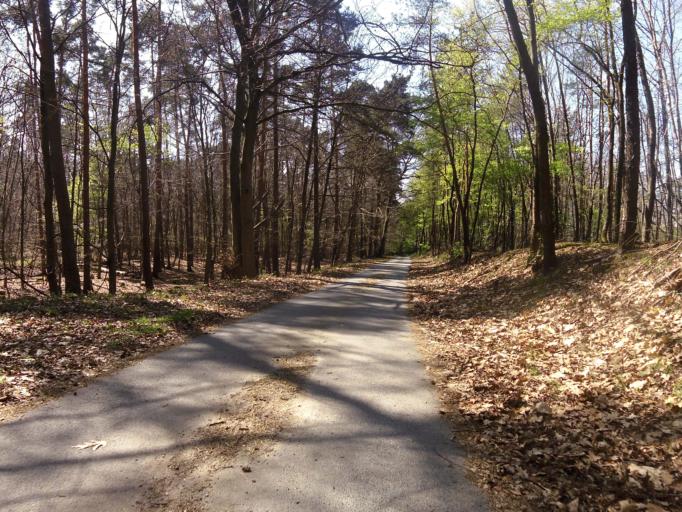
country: DE
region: Hesse
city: Kelsterbach
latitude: 50.0198
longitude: 8.5030
